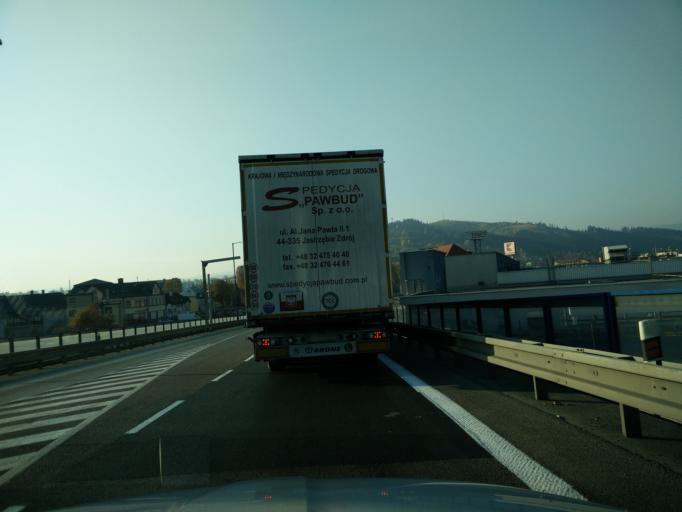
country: SK
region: Zilinsky
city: Cadca
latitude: 49.4400
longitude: 18.7921
